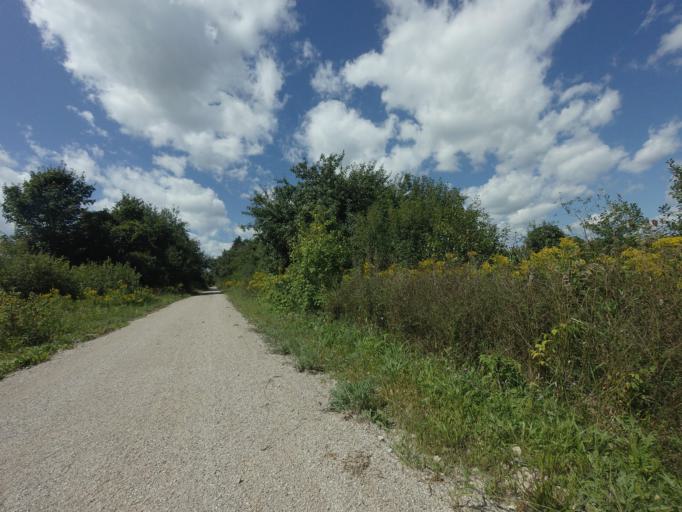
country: CA
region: Ontario
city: Huron East
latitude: 43.6269
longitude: -81.1702
